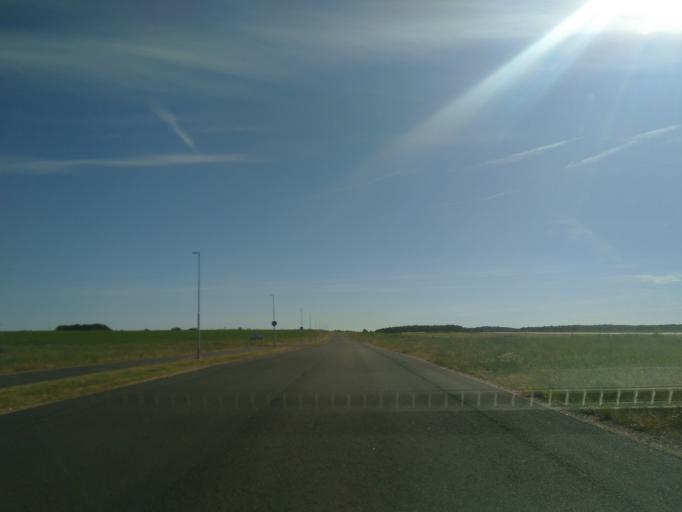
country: SE
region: Vaestra Goetaland
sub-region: Vargarda Kommun
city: Vargarda
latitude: 58.0401
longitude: 12.7892
